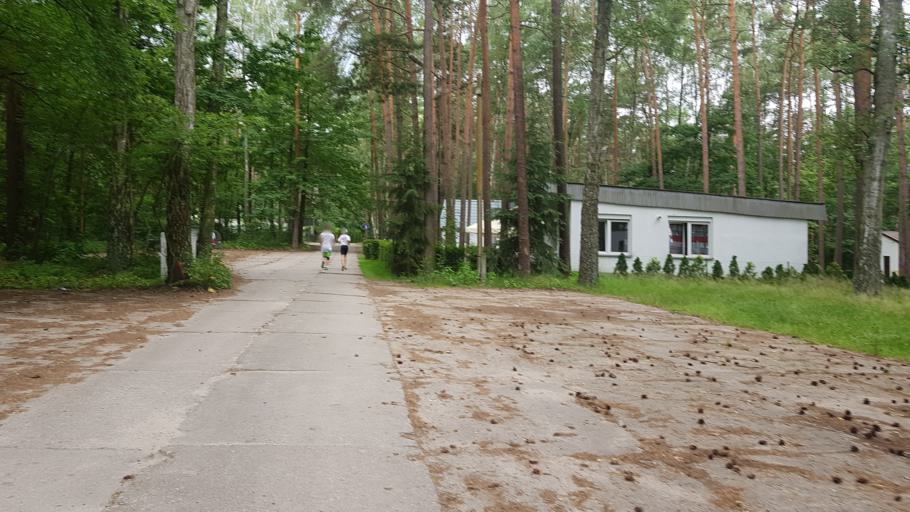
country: PL
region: Opole Voivodeship
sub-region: Powiat opolski
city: Chrzastowice
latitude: 50.7085
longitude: 18.1252
